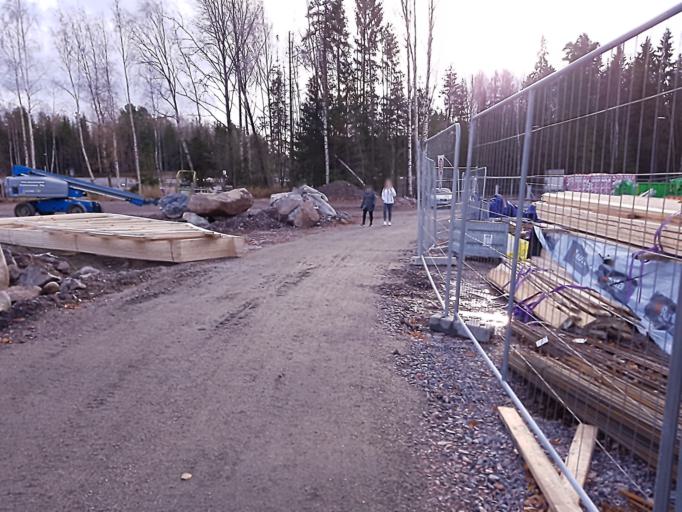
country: FI
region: Uusimaa
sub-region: Helsinki
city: Teekkarikylae
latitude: 60.2607
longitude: 24.8942
